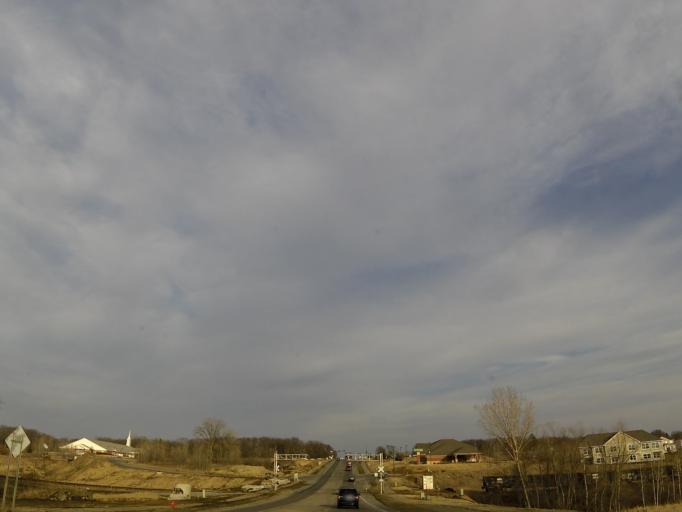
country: US
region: Minnesota
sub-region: Dakota County
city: Lakeville
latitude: 44.6813
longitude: -93.2837
